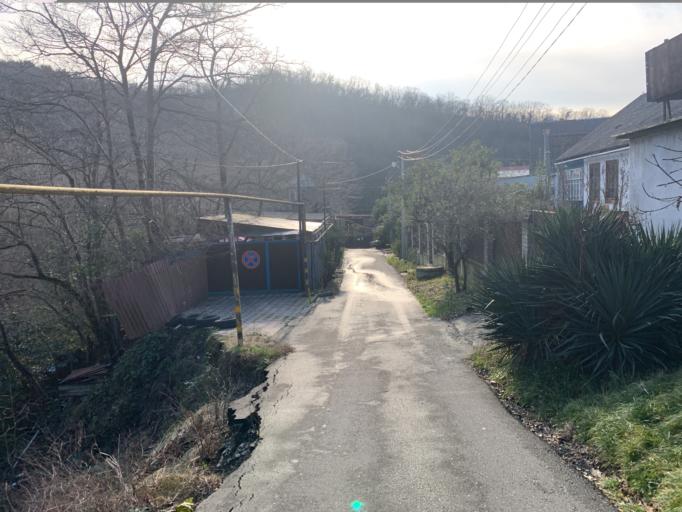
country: RU
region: Krasnodarskiy
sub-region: Sochi City
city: Lazarevskoye
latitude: 43.9237
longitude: 39.3233
